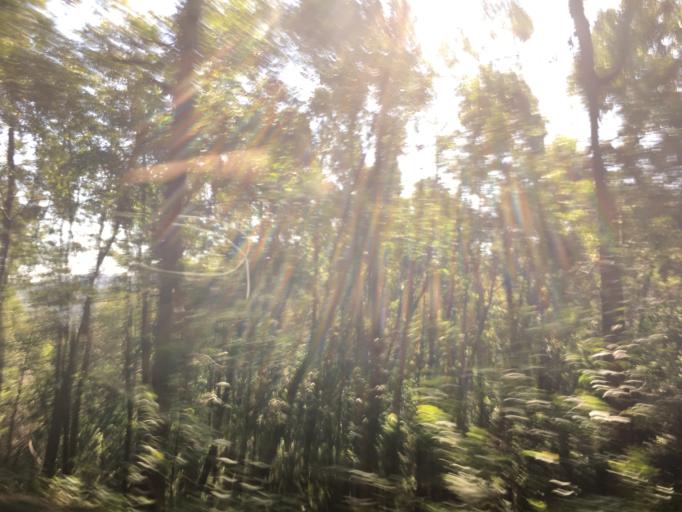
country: PT
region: Lisbon
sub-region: Sintra
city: Colares
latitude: 38.7724
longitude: -9.4360
